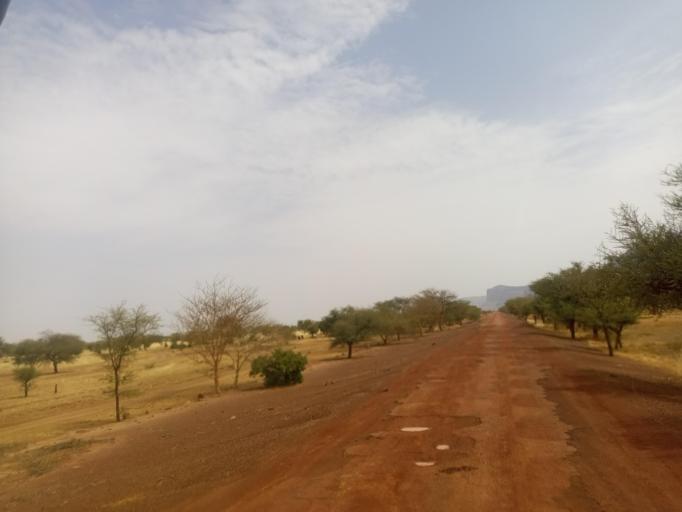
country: ML
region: Mopti
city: Douentza
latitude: 15.1245
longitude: -2.2274
